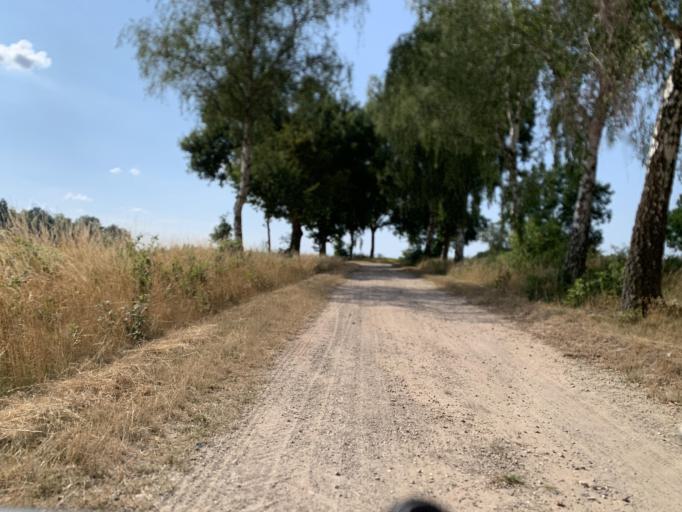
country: DE
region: Lower Saxony
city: Thomasburg
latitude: 53.2316
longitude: 10.6425
